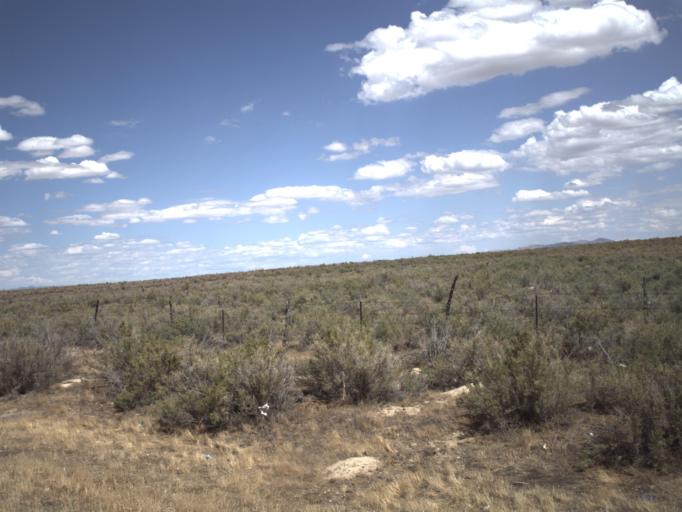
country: US
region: Utah
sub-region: Millard County
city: Delta
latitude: 39.3451
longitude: -112.4944
